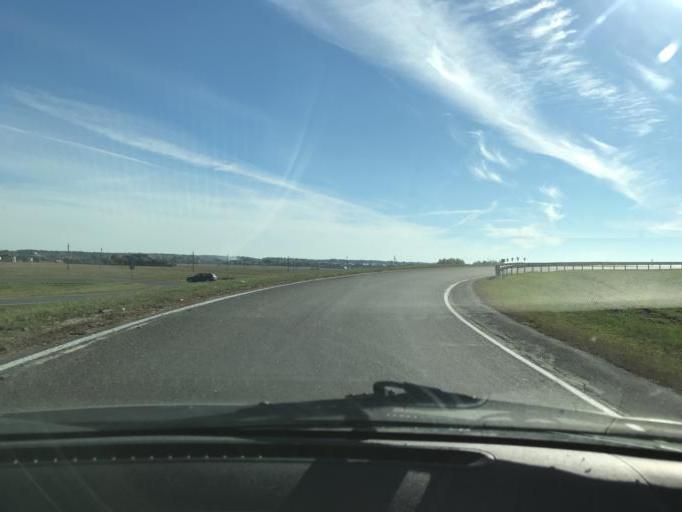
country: BY
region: Brest
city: Ivatsevichy
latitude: 52.6995
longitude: 25.3645
